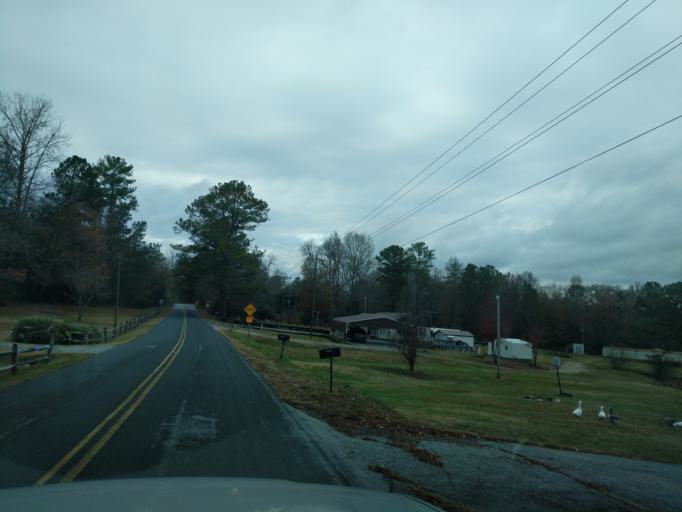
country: US
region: South Carolina
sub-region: Laurens County
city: Clinton
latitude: 34.4056
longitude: -81.9408
